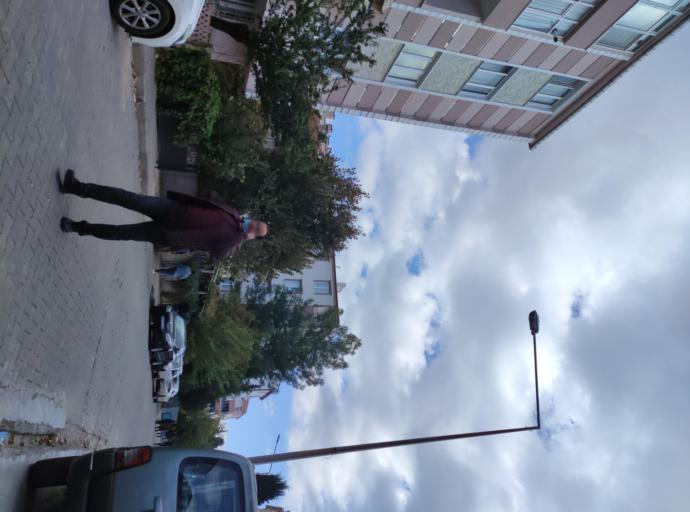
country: TR
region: Kirklareli
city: Luleburgaz
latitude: 41.4063
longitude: 27.3652
